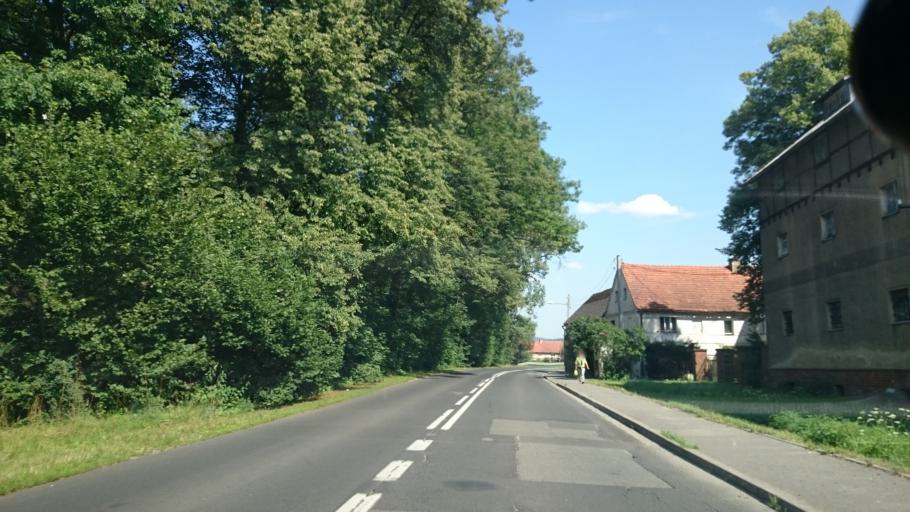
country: PL
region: Lower Silesian Voivodeship
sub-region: Powiat klodzki
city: Ladek-Zdroj
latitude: 50.3465
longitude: 16.7785
